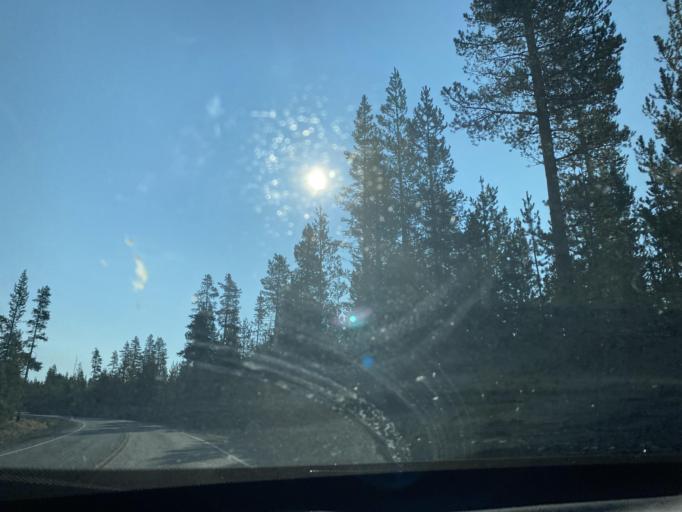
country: US
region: Oregon
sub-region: Deschutes County
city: Three Rivers
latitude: 43.7058
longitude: -121.2907
